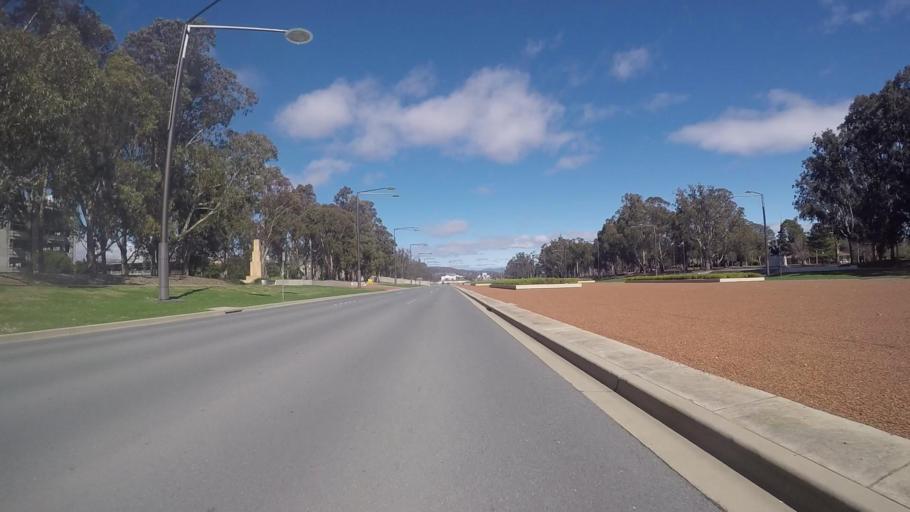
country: AU
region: Australian Capital Territory
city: Canberra
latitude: -35.2872
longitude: 149.1434
